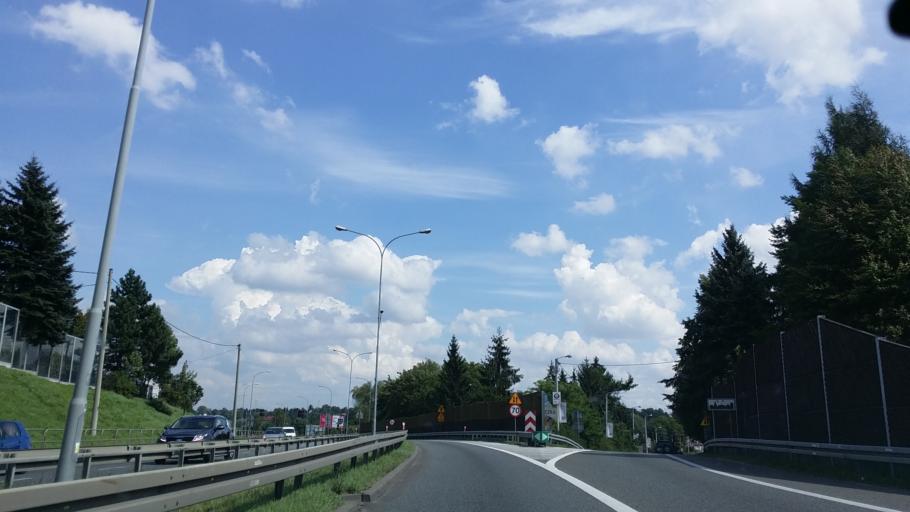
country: PL
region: Lesser Poland Voivodeship
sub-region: Powiat wielicki
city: Wieliczka
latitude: 49.9945
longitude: 20.0393
